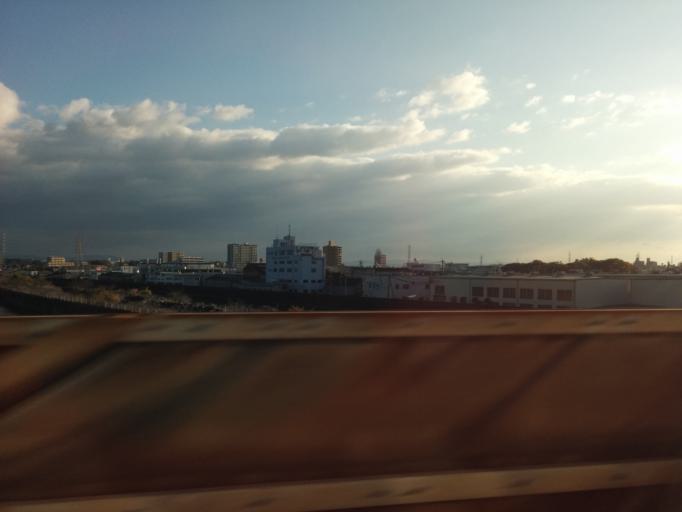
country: JP
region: Aichi
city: Obu
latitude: 35.0754
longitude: 136.9372
